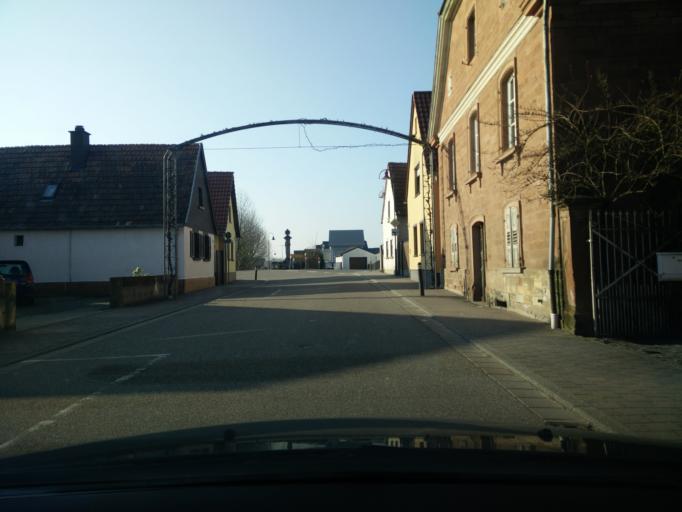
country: DE
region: Rheinland-Pfalz
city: Steinweiler
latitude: 49.1193
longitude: 8.1413
